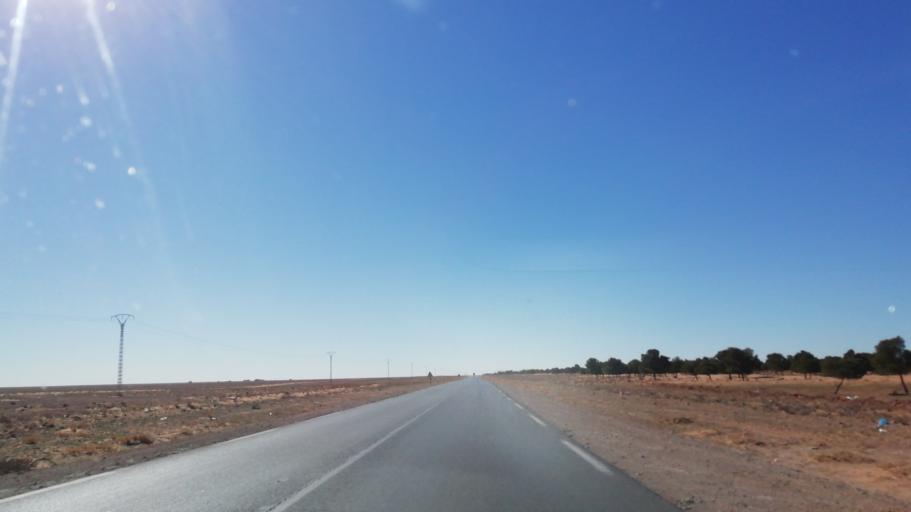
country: DZ
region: Saida
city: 'Ain el Hadjar
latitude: 34.0000
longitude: 0.0427
